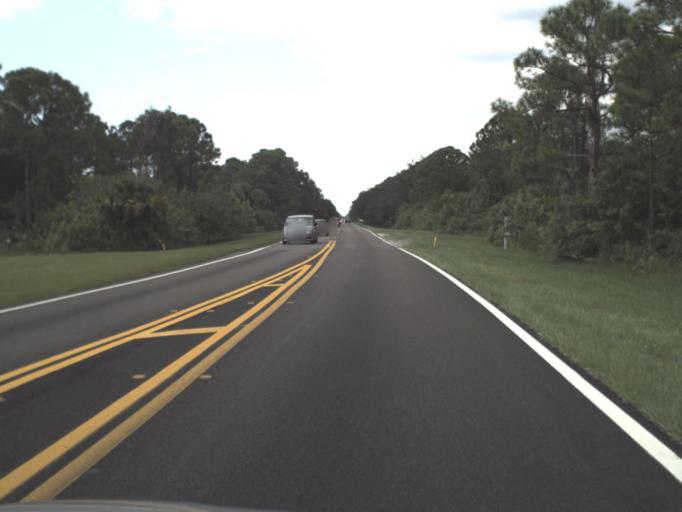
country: US
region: Florida
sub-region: Sarasota County
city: Warm Mineral Springs
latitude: 27.0496
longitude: -82.3064
